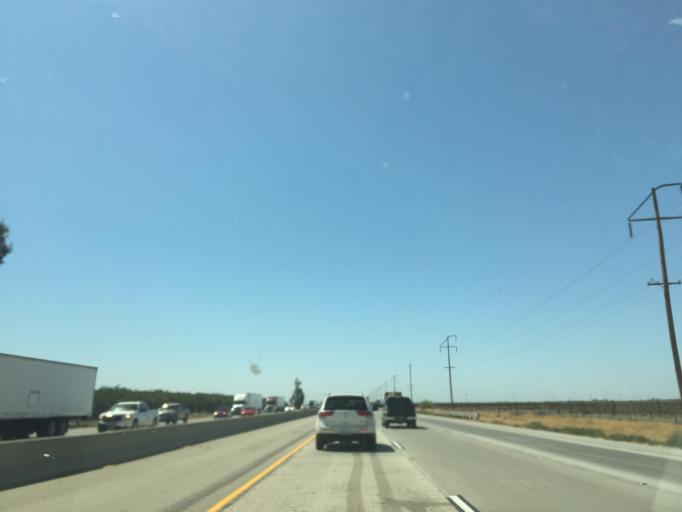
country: US
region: California
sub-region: Kern County
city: Rosedale
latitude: 35.4738
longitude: -119.1300
